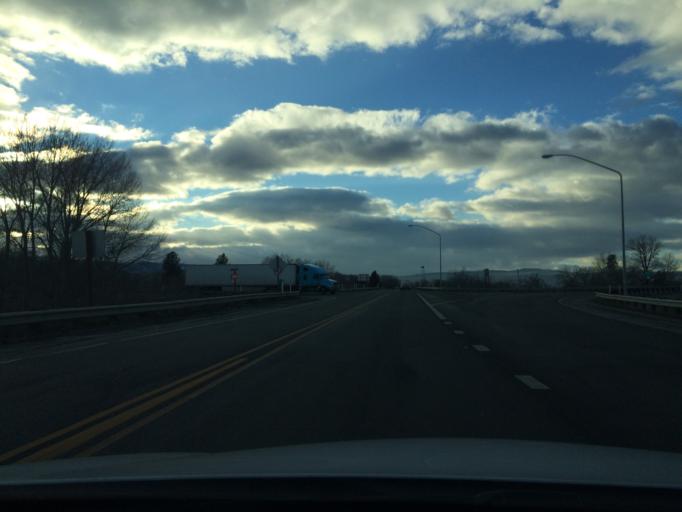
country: US
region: Washington
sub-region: Kittitas County
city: Ellensburg
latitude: 47.0063
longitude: -120.5883
